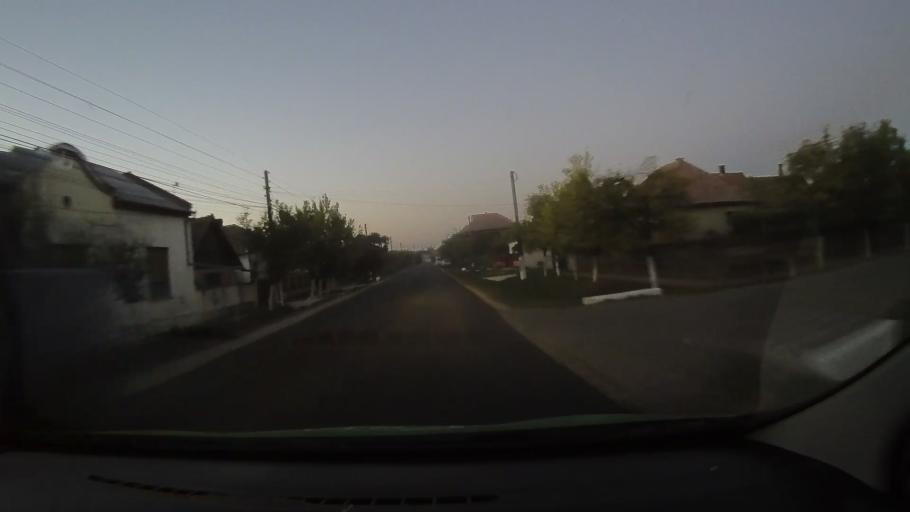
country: RO
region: Bihor
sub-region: Comuna Simian
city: Simian
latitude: 47.4985
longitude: 22.0911
